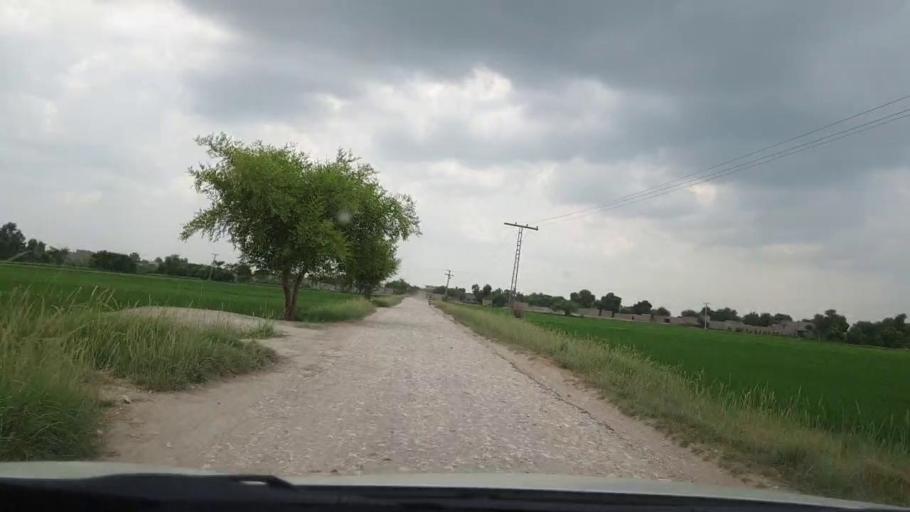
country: PK
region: Sindh
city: Dokri
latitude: 27.3302
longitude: 68.1025
